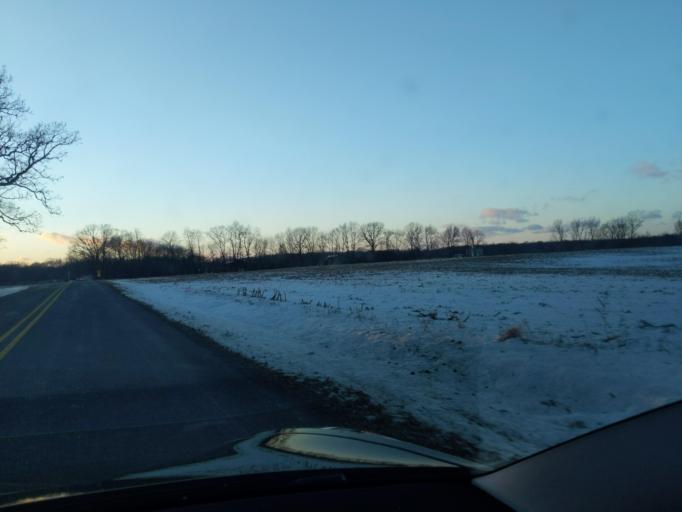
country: US
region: Michigan
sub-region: Ingham County
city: Stockbridge
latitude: 42.4681
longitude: -84.2798
